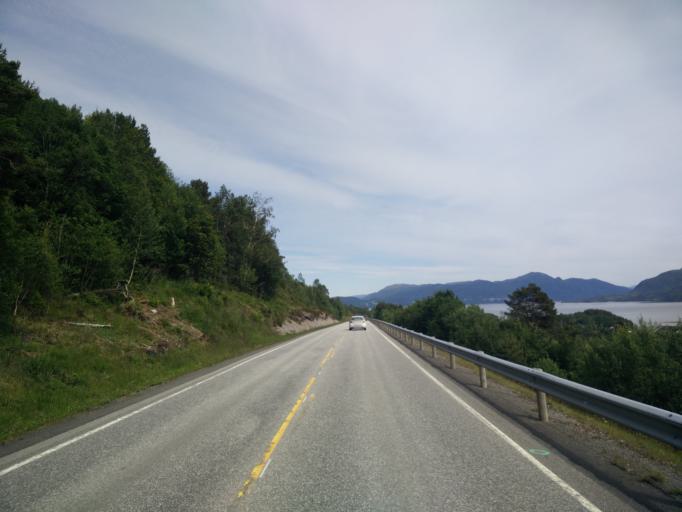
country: NO
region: More og Romsdal
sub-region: Kristiansund
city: Rensvik
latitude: 62.9729
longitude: 7.8347
